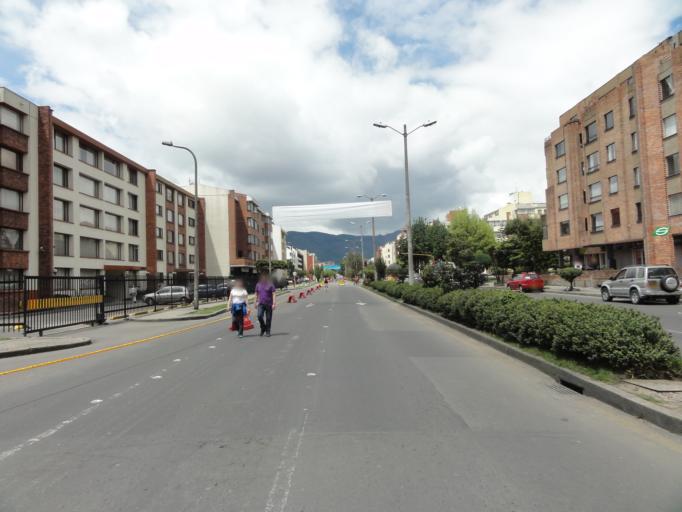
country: CO
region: Bogota D.C.
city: Barrio San Luis
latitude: 4.7009
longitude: -74.0631
